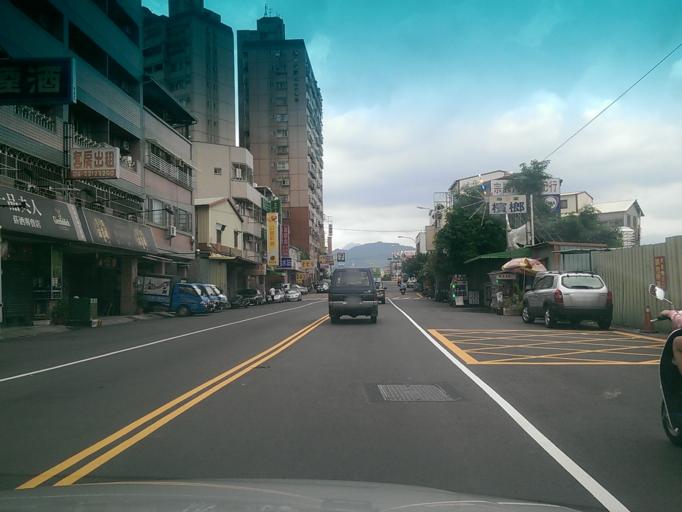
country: TW
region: Taiwan
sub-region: Taichung City
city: Taichung
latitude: 24.1389
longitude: 120.6983
